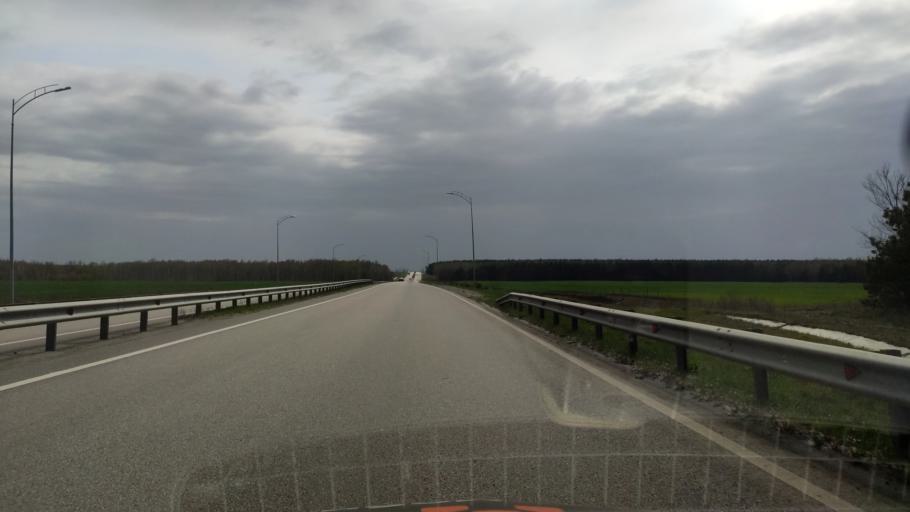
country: RU
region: Belgorod
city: Staryy Oskol
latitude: 51.4079
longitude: 37.8809
